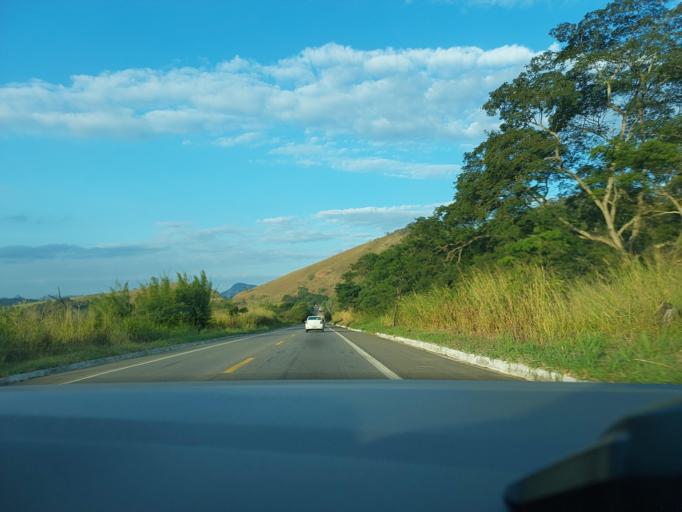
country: BR
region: Minas Gerais
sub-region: Muriae
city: Muriae
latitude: -21.1271
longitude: -42.2421
